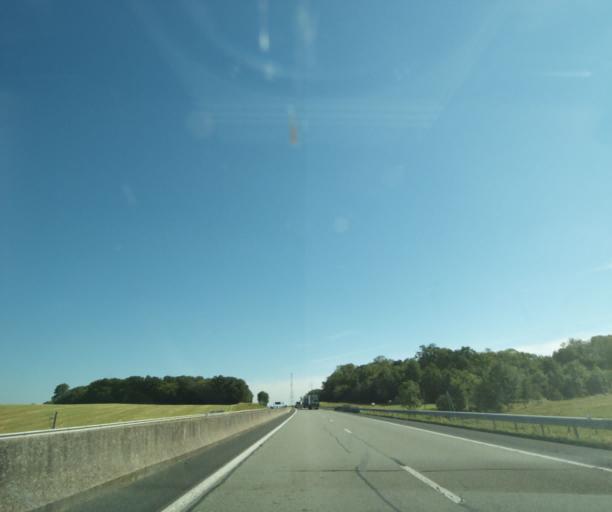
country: FR
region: Lorraine
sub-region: Departement des Vosges
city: Lamarche
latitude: 48.1104
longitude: 5.6568
